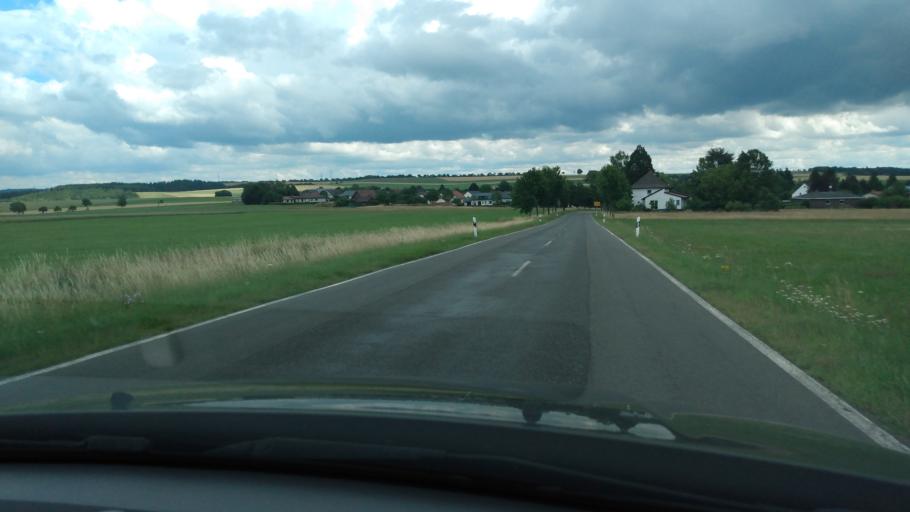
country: DE
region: Rheinland-Pfalz
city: Grosslittgen
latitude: 50.0317
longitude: 6.7936
